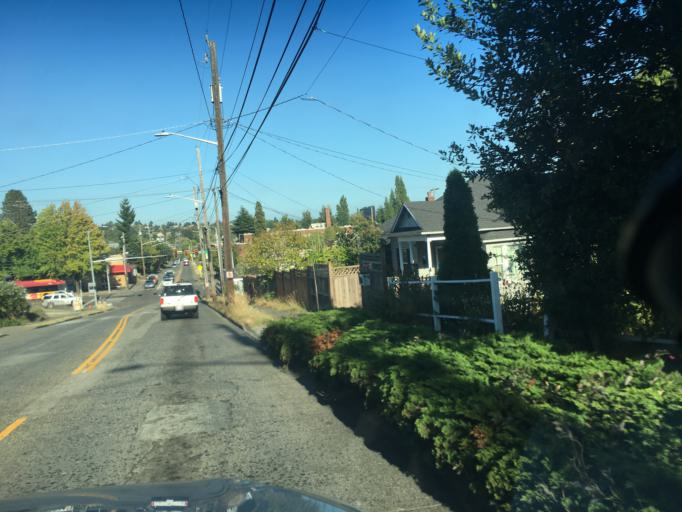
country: US
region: Washington
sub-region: King County
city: Shoreline
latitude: 47.6869
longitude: -122.3459
